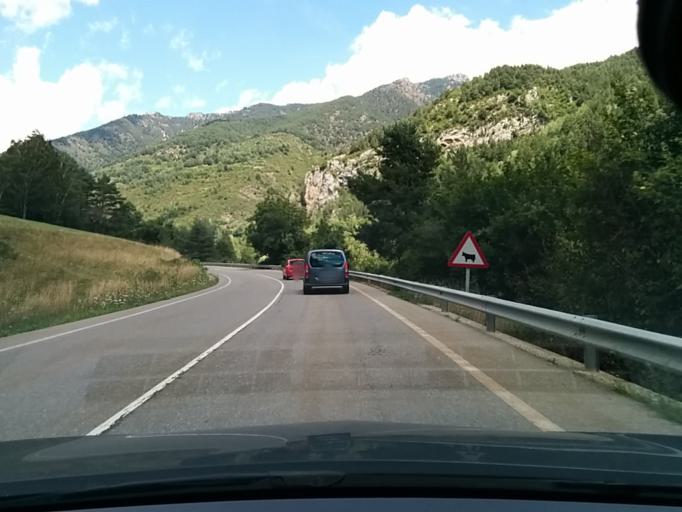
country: ES
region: Aragon
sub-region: Provincia de Huesca
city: Bielsa
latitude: 42.6198
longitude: 0.2311
